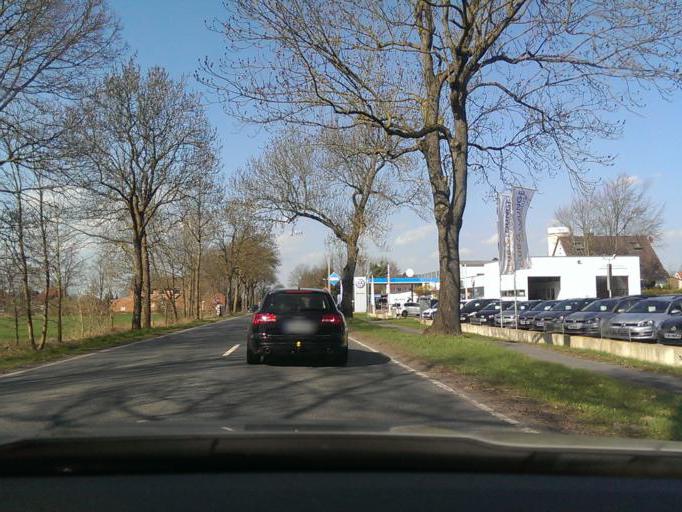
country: DE
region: Lower Saxony
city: Elze
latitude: 52.5762
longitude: 9.7277
